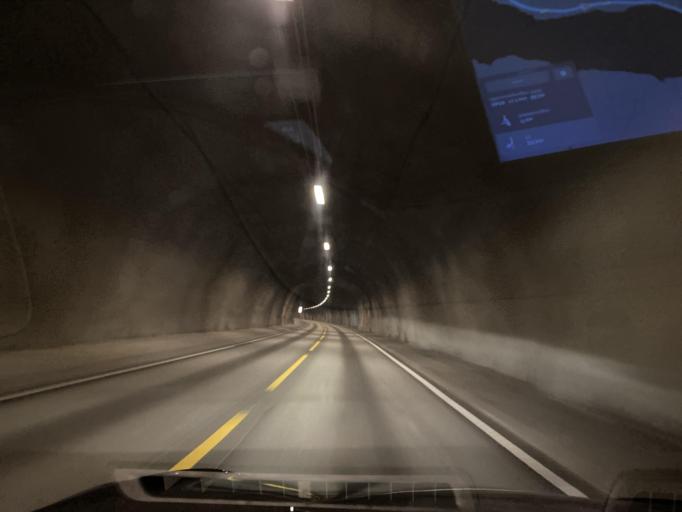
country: NO
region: Rogaland
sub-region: Sauda
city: Sauda
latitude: 59.8305
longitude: 6.2635
